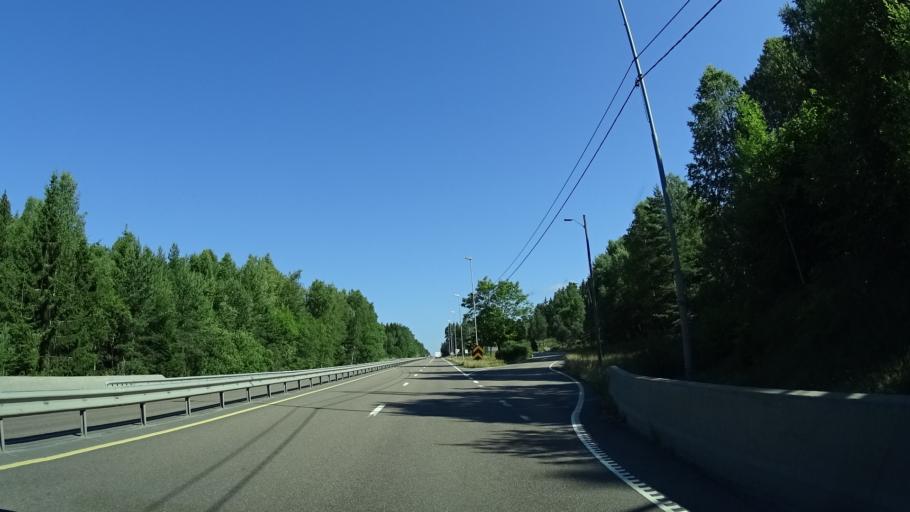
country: NO
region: Akershus
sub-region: Oppegard
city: Kolbotn
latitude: 59.7874
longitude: 10.7613
